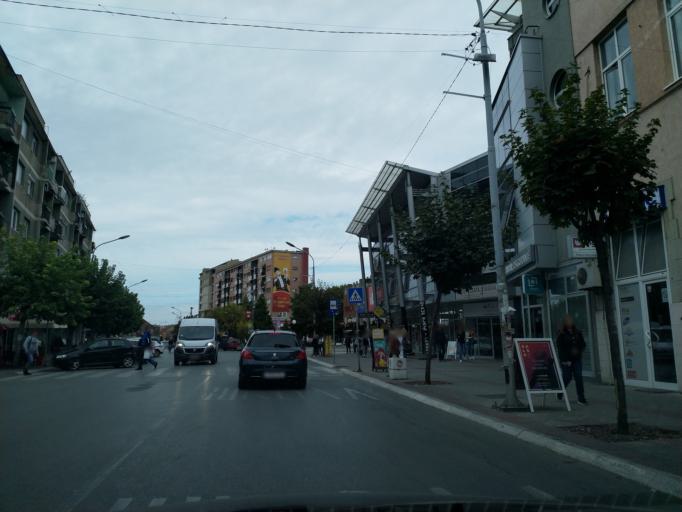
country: RS
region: Central Serbia
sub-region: Pomoravski Okrug
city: Jagodina
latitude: 43.9785
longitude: 21.2609
